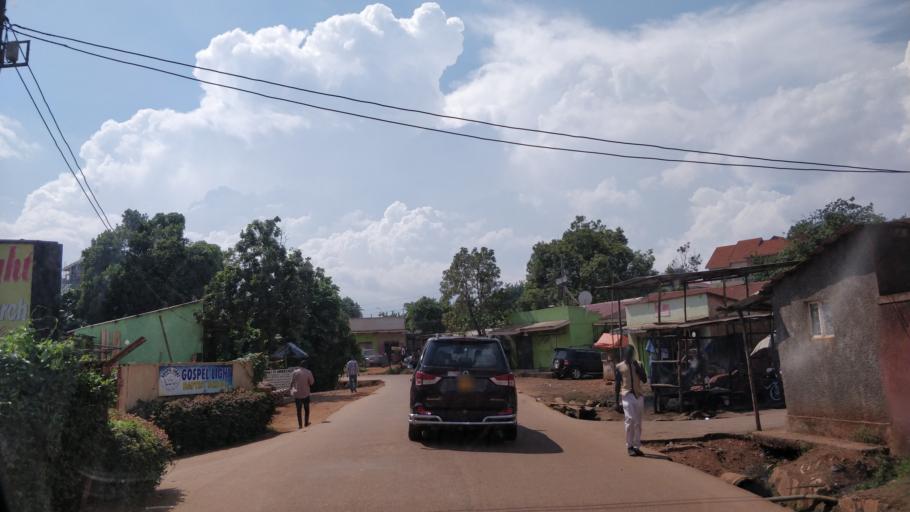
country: UG
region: Central Region
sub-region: Kampala District
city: Kampala
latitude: 0.2834
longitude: 32.6121
